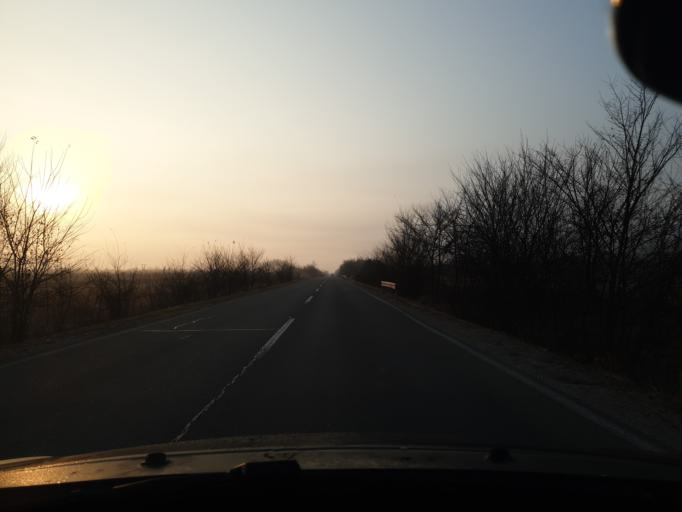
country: RS
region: Central Serbia
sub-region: Jablanicki Okrug
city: Leskovac
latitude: 42.9634
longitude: 21.9810
